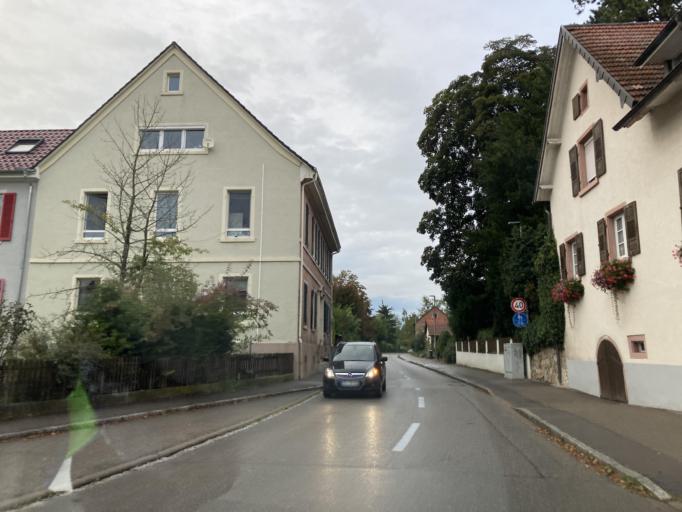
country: DE
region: Baden-Wuerttemberg
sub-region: Freiburg Region
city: Mullheim
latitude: 47.7932
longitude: 7.6213
